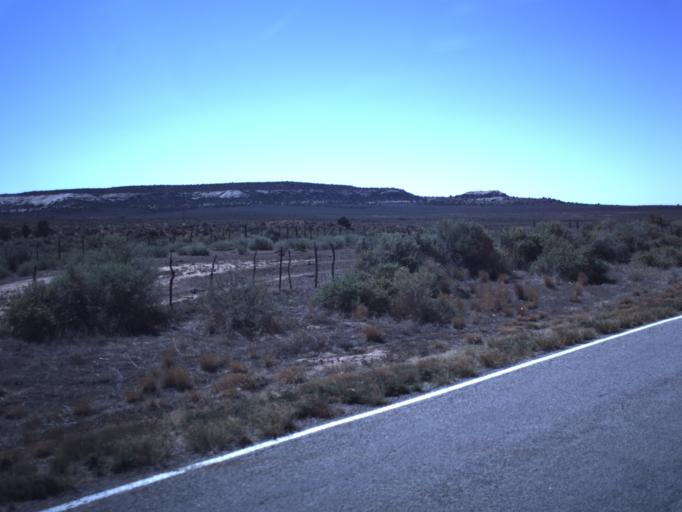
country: US
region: Utah
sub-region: Grand County
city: Moab
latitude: 38.3051
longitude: -109.3675
